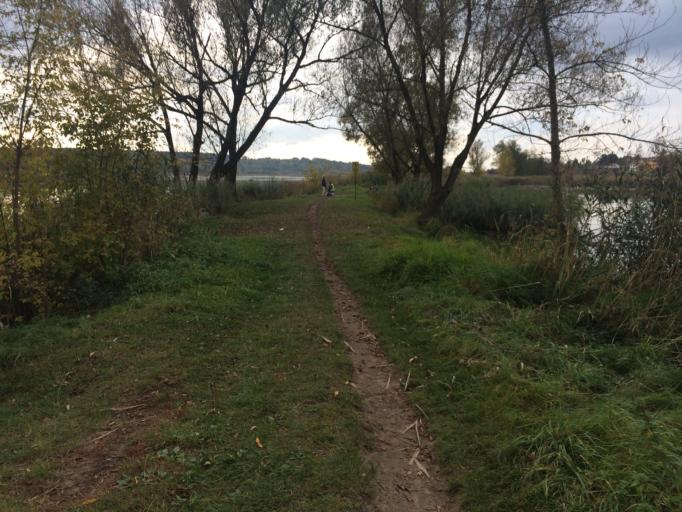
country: PL
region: Swietokrzyskie
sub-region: Powiat starachowicki
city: Starachowice
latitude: 51.0484
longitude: 21.0590
